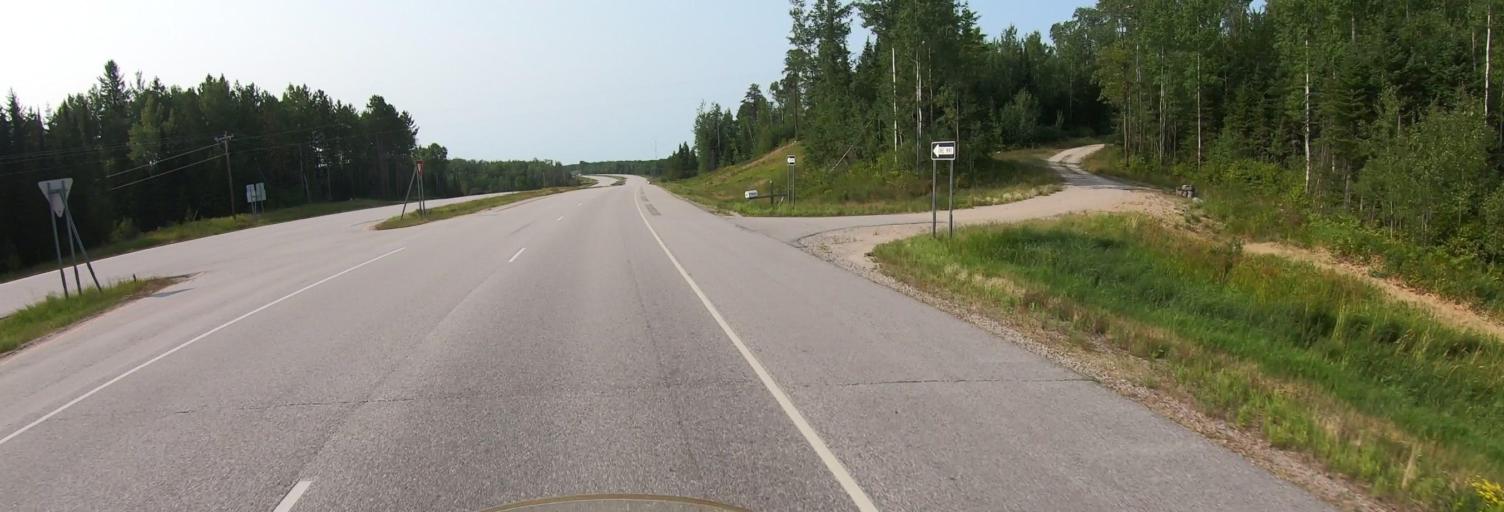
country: US
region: Minnesota
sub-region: Saint Louis County
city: Mountain Iron
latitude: 47.7751
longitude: -92.6549
